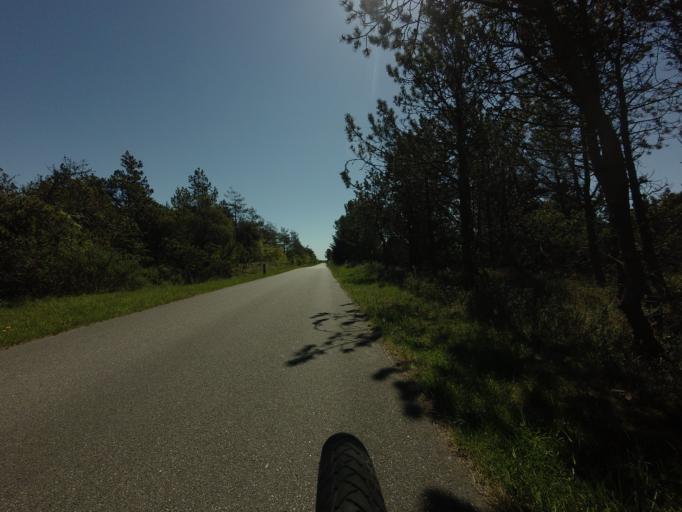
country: DK
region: North Denmark
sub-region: Jammerbugt Kommune
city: Kas
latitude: 57.2227
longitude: 9.5735
